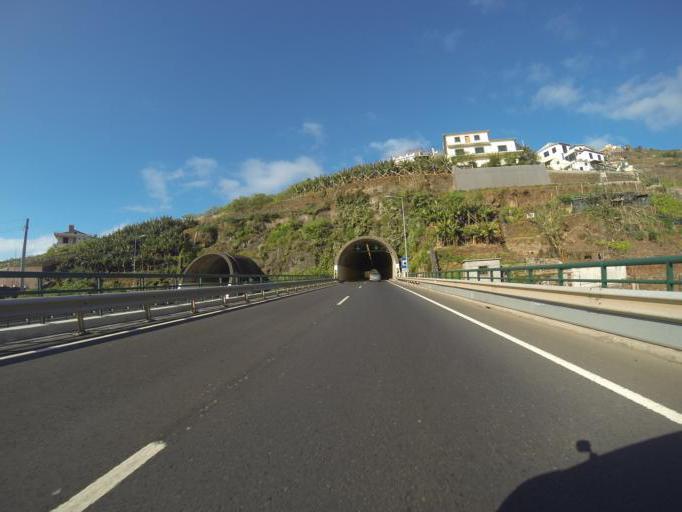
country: PT
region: Madeira
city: Camara de Lobos
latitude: 32.6617
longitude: -16.9822
